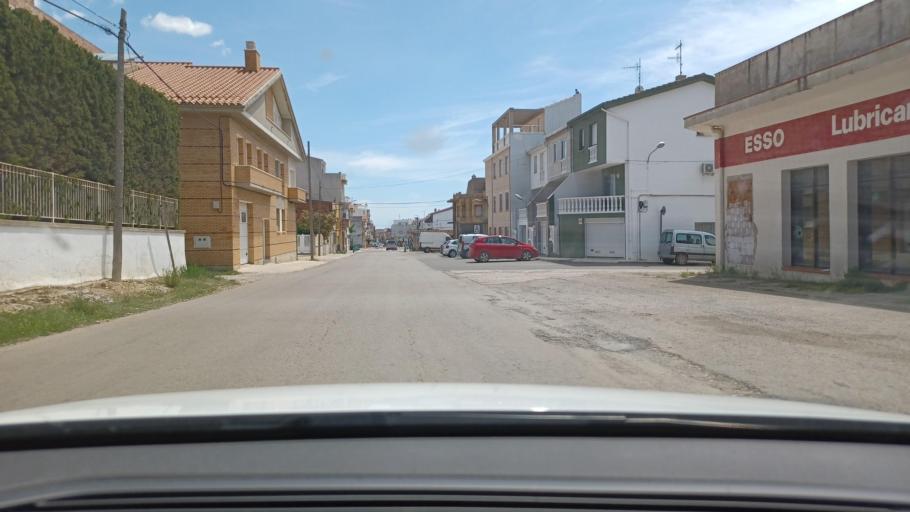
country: ES
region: Valencia
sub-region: Provincia de Castello
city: Rosell
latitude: 40.6400
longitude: 0.2783
